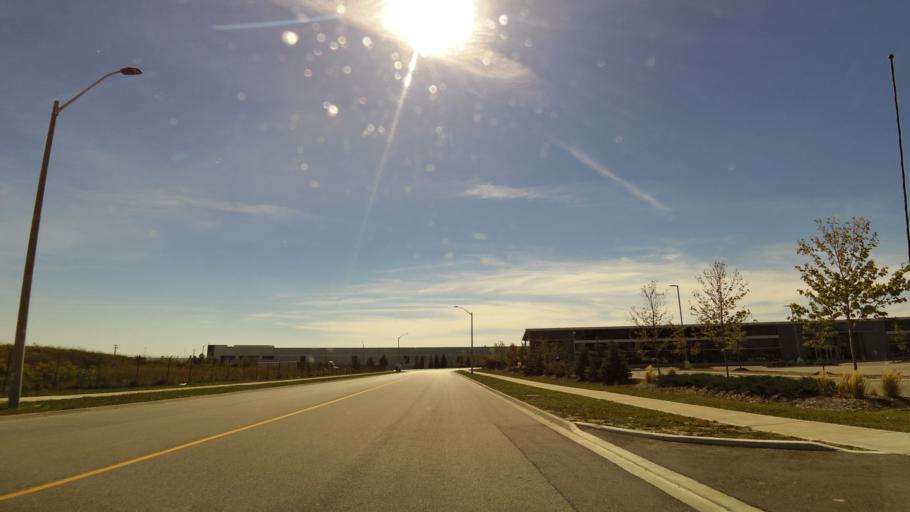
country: CA
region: Ontario
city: Mississauga
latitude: 43.6341
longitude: -79.6928
